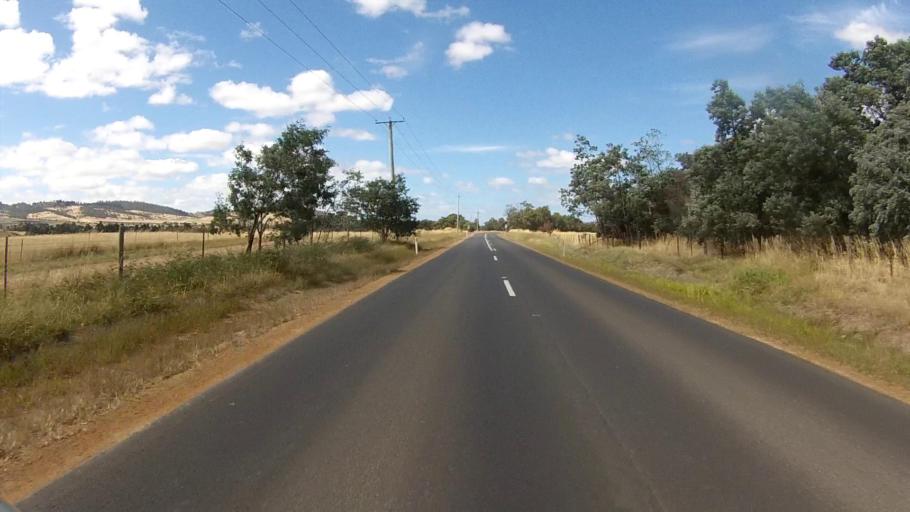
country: AU
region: Tasmania
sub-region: Clarence
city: Cambridge
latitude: -42.7222
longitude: 147.4347
